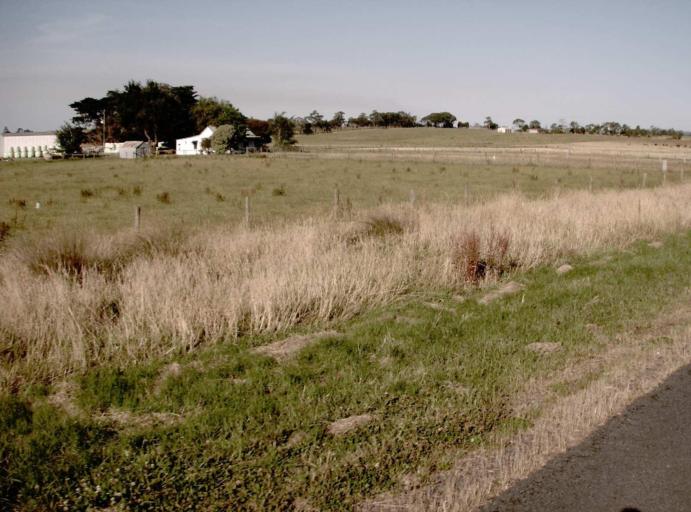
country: AU
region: Victoria
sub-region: Latrobe
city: Morwell
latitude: -38.3324
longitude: 146.3572
